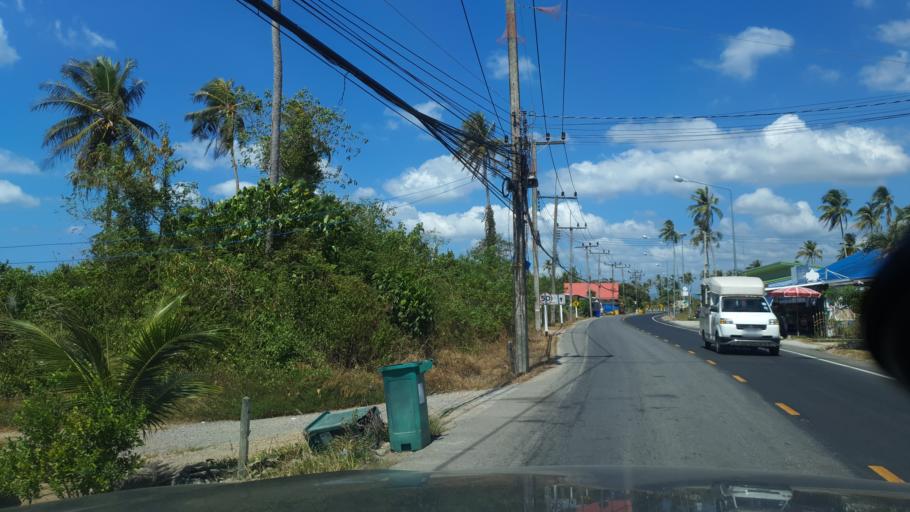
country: TH
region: Phuket
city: Thalang
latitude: 8.1408
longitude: 98.3064
